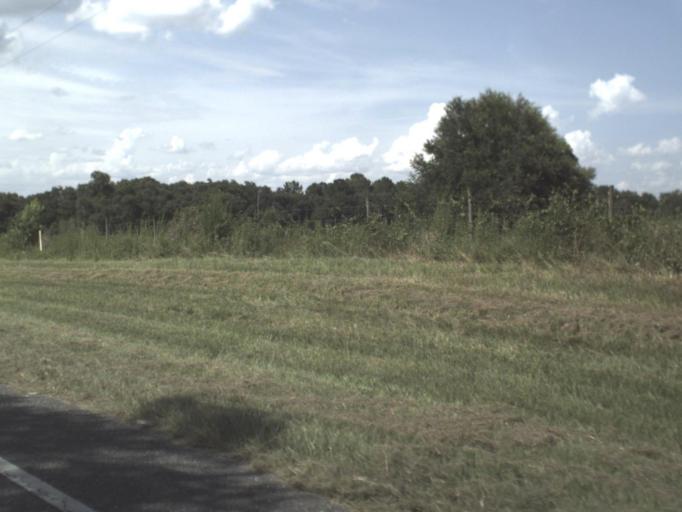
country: US
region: Florida
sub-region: Alachua County
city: High Springs
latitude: 29.9502
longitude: -82.7133
